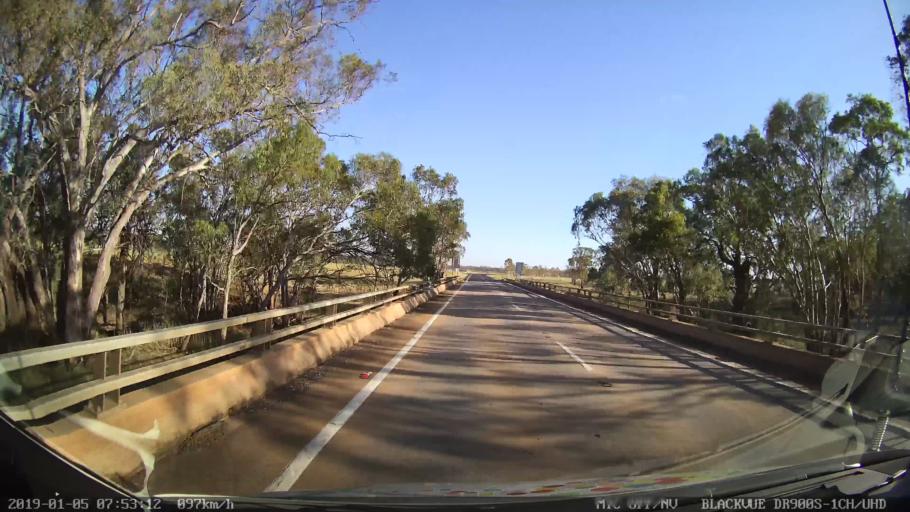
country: AU
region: New South Wales
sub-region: Gilgandra
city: Gilgandra
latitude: -31.7475
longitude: 148.6411
